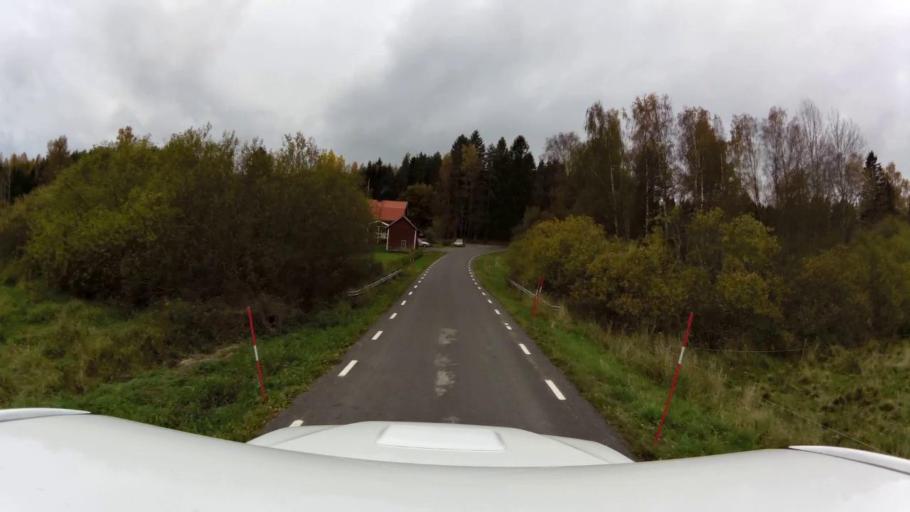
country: SE
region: OEstergoetland
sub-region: Linkopings Kommun
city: Ljungsbro
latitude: 58.5694
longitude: 15.4590
